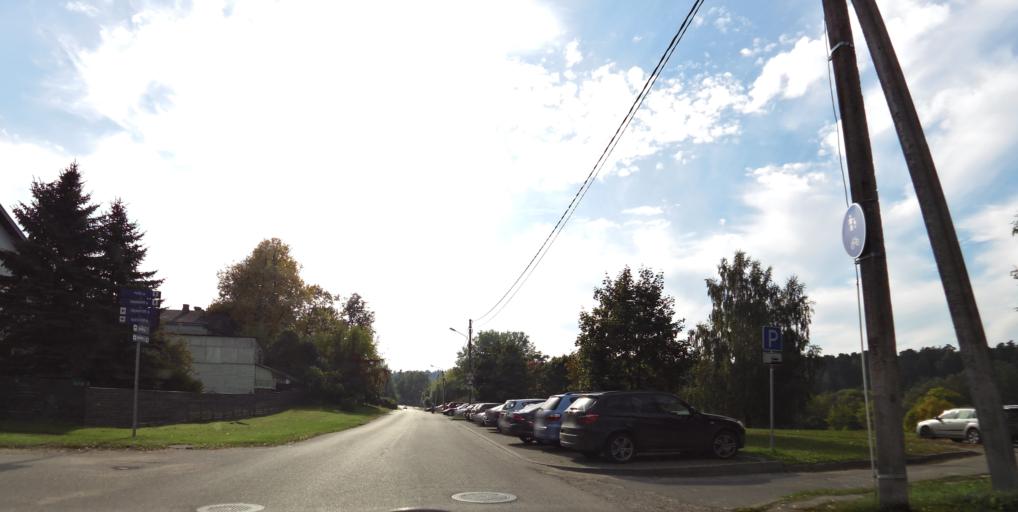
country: LT
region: Vilnius County
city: Seskine
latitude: 54.6920
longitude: 25.2460
